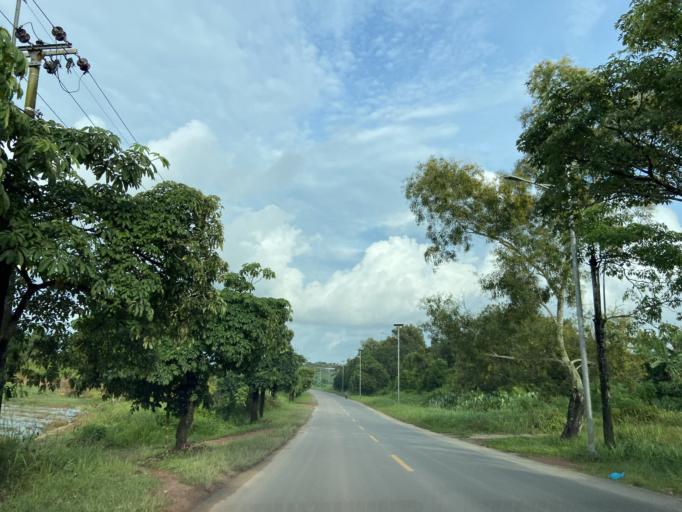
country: ID
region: Riau Islands
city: Tanjungpinang
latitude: 0.9355
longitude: 104.1044
